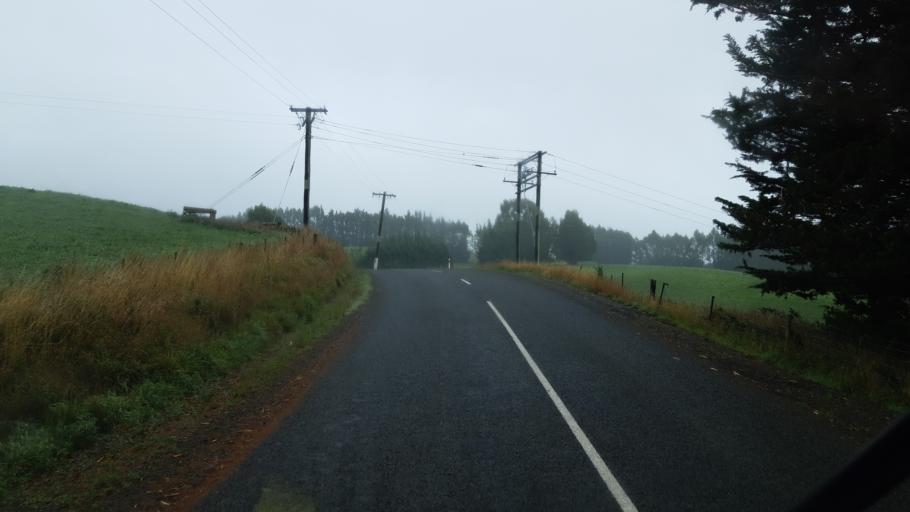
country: NZ
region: Otago
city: Oamaru
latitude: -44.9397
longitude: 170.7560
